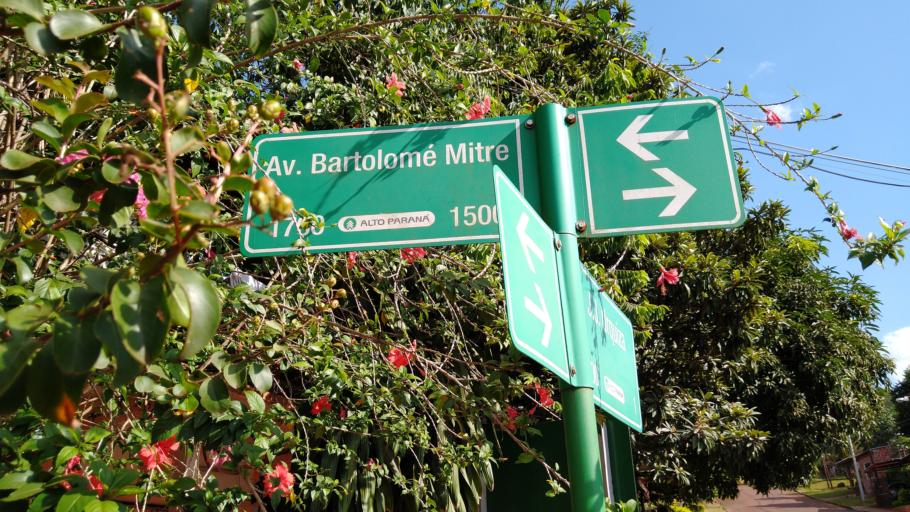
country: AR
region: Misiones
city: Puerto Piray
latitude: -26.4686
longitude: -54.7100
